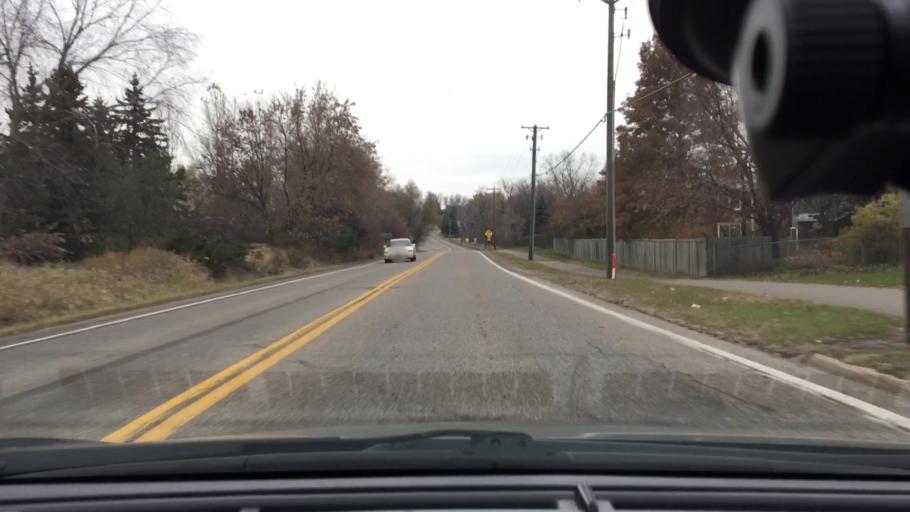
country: US
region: Minnesota
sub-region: Hennepin County
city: Corcoran
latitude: 45.1071
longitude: -93.5118
